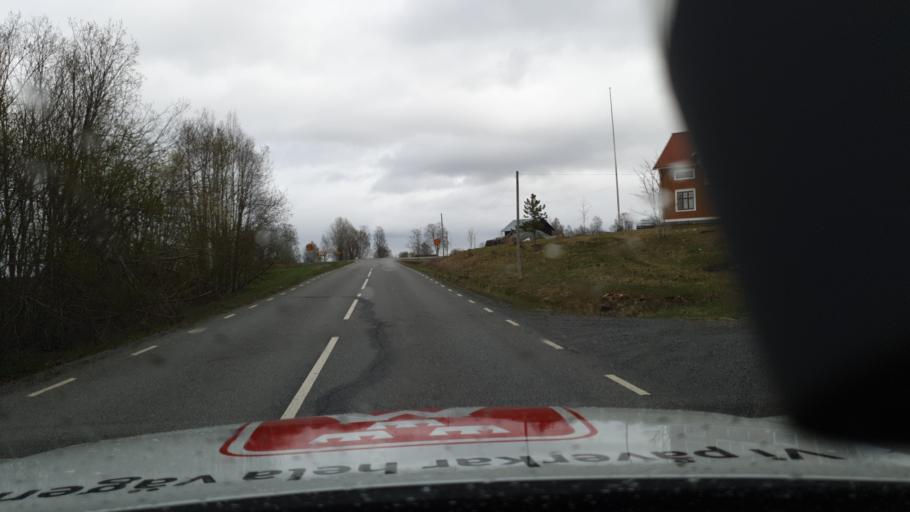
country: SE
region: Jaemtland
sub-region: Stroemsunds Kommun
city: Stroemsund
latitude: 63.6295
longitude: 15.2279
